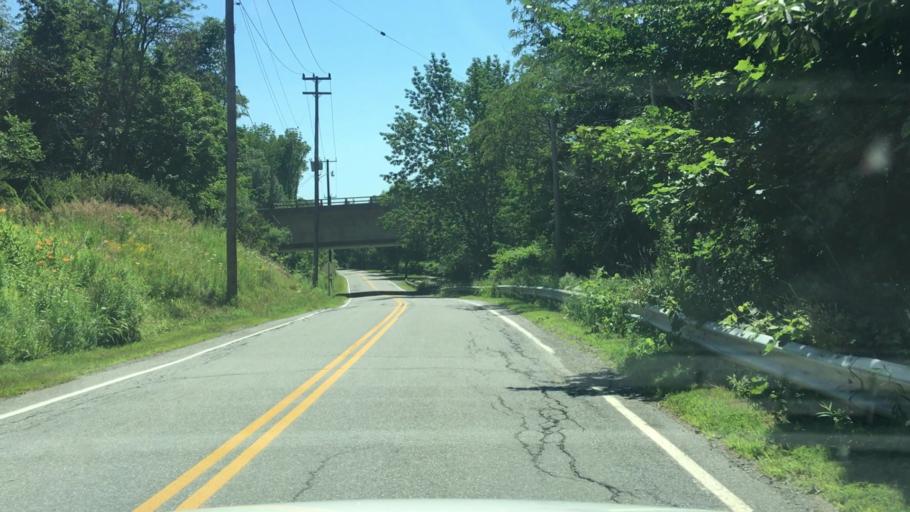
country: US
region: Maine
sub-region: Penobscot County
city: Bangor
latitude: 44.8155
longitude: -68.7892
